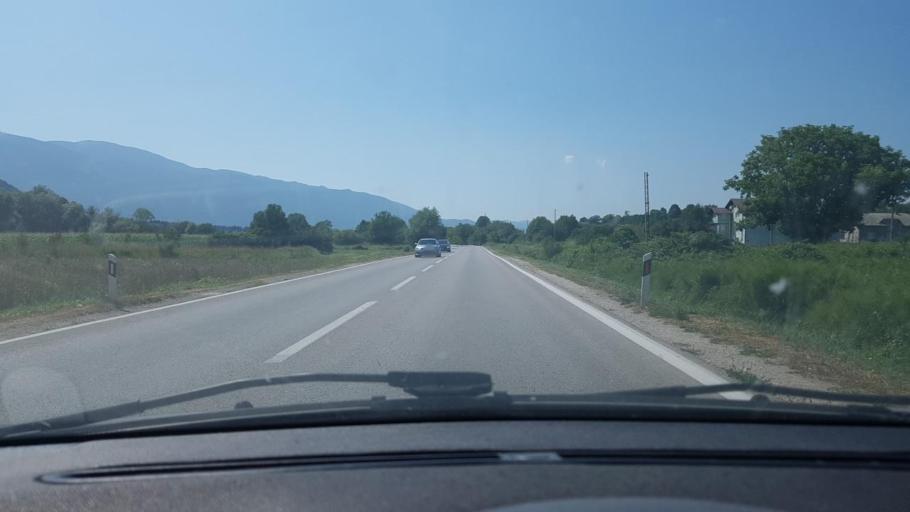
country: BA
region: Federation of Bosnia and Herzegovina
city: Bihac
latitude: 44.8061
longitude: 15.8950
